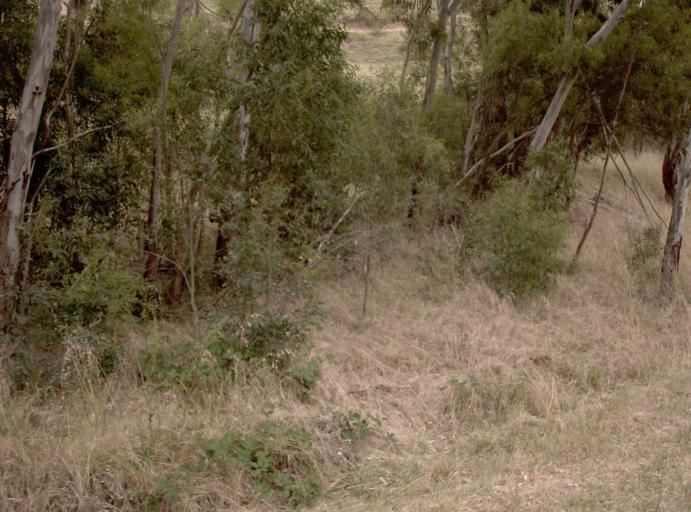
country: AU
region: Victoria
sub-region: Wellington
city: Heyfield
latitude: -37.6873
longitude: 146.6553
